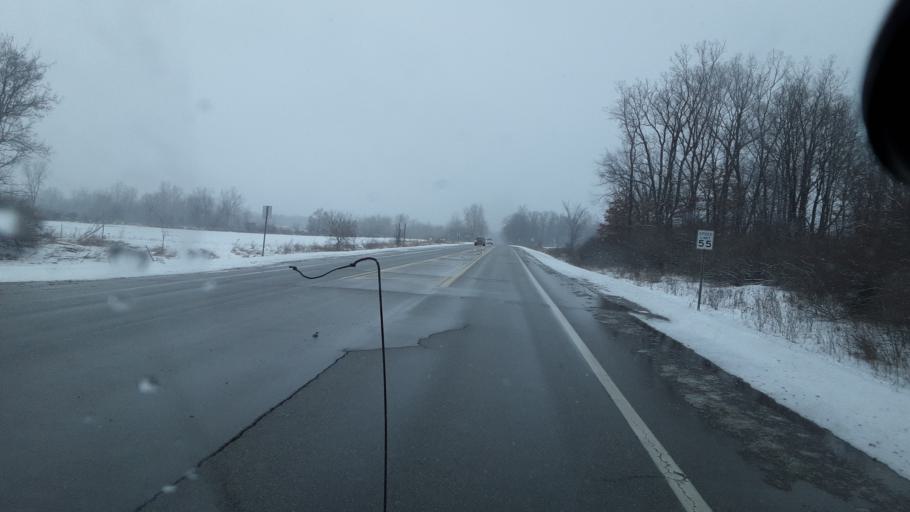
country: US
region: Michigan
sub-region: Jackson County
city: Jackson
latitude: 42.3146
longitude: -84.3840
